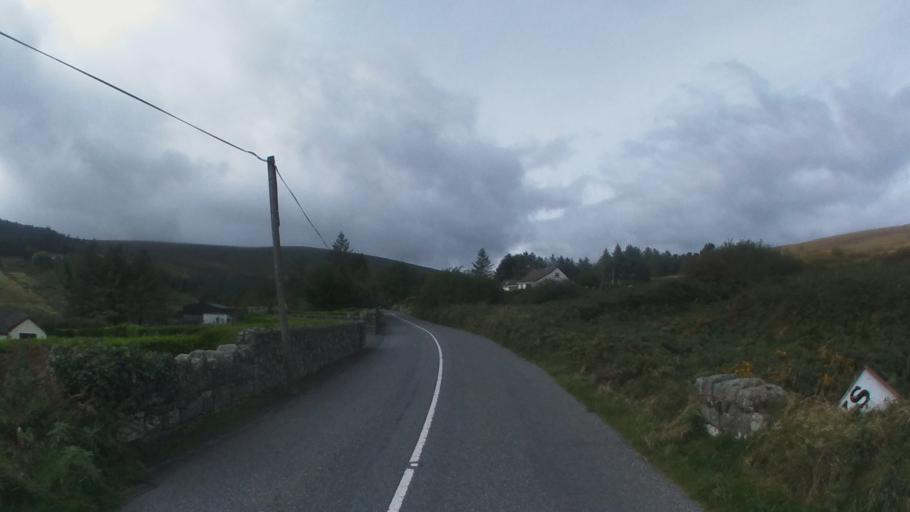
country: IE
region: Leinster
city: Ballinteer
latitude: 53.2248
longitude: -6.2441
